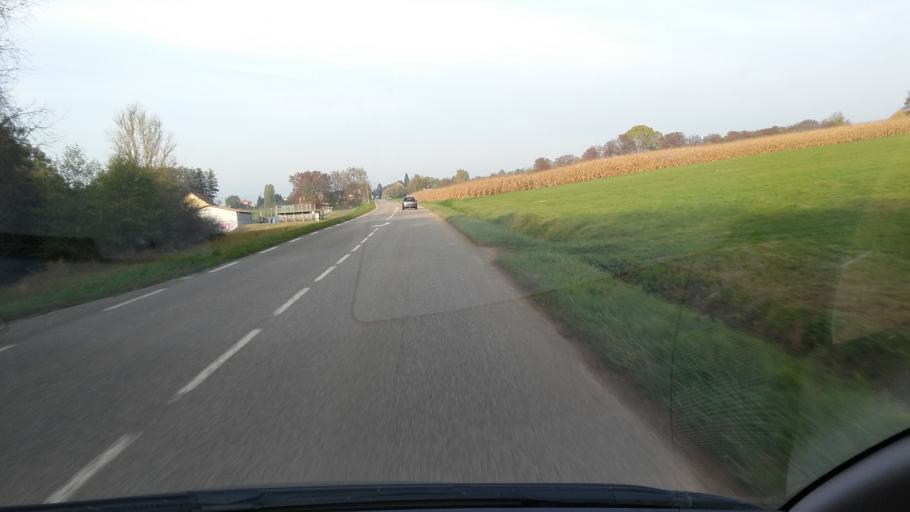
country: FR
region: Lorraine
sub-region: Departement de la Moselle
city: Phalsbourg
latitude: 48.7595
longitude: 7.2466
